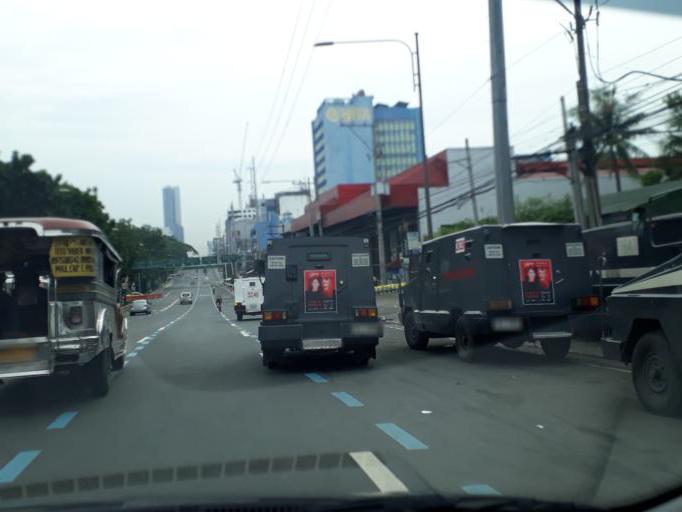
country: PH
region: Calabarzon
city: Del Monte
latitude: 14.6336
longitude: 121.0207
